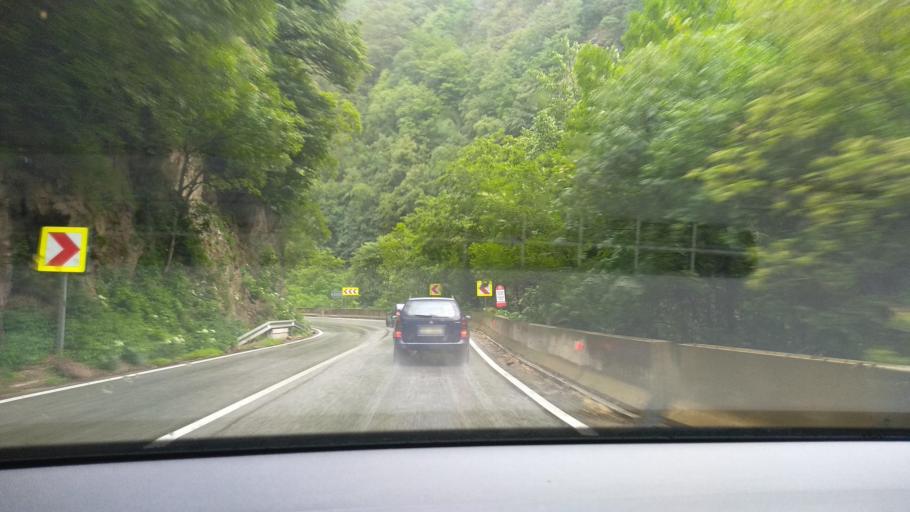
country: RO
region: Hunedoara
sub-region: Comuna Aninoasa
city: Iscroni
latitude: 45.3036
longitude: 23.3830
